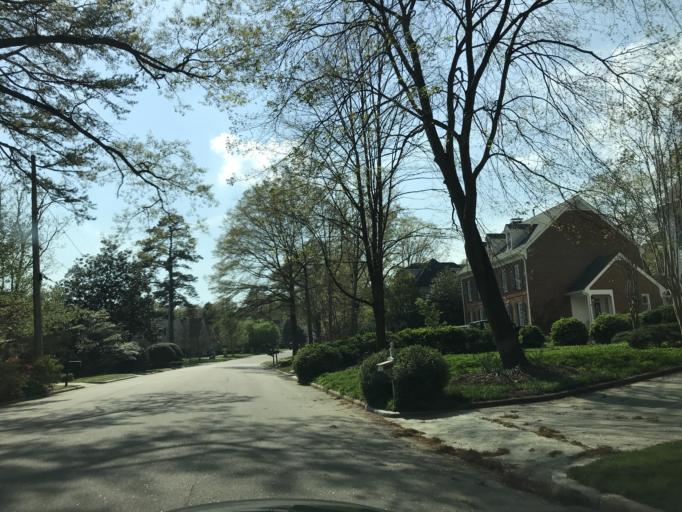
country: US
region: North Carolina
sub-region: Wake County
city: West Raleigh
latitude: 35.8060
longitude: -78.6809
